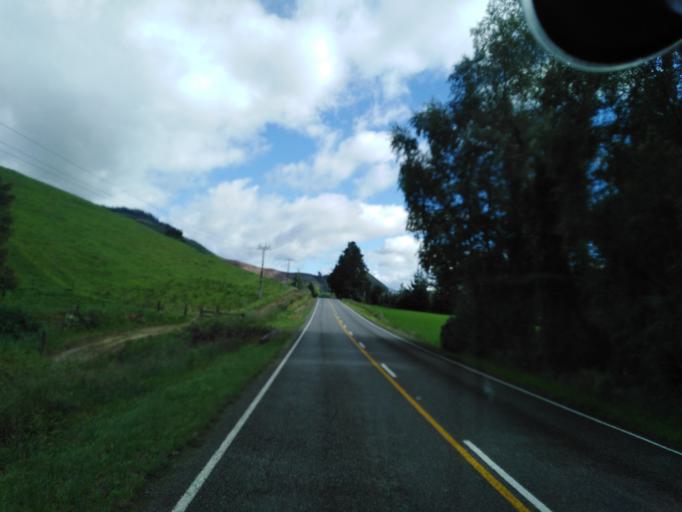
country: NZ
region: Nelson
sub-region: Nelson City
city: Nelson
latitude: -41.2753
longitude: 173.5730
